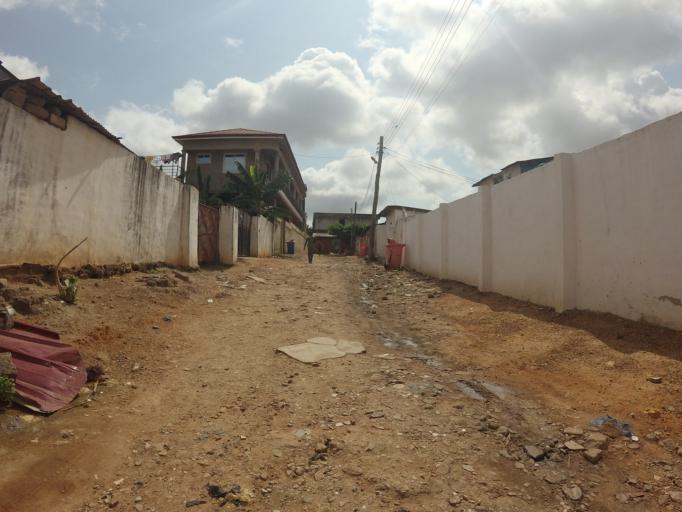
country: GH
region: Greater Accra
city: Dome
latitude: 5.6170
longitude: -0.2464
